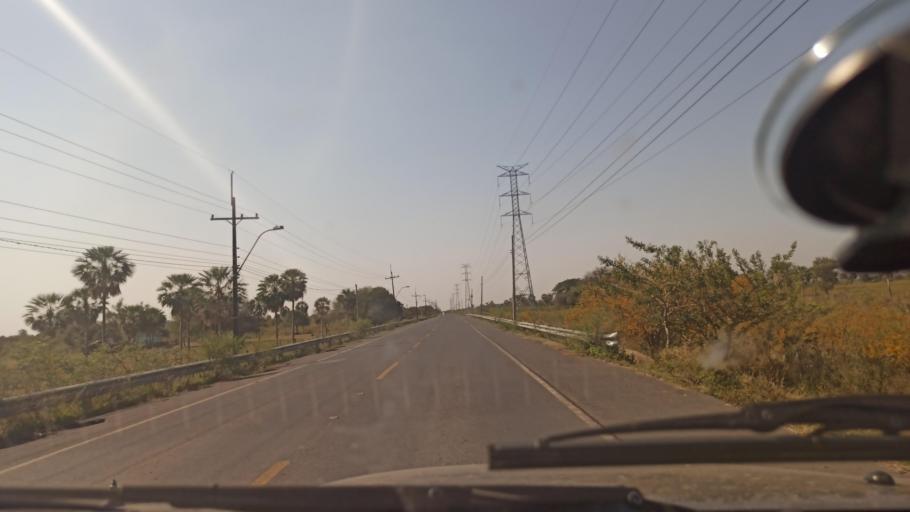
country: PY
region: Presidente Hayes
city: Nanawa
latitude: -25.2559
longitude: -57.6769
